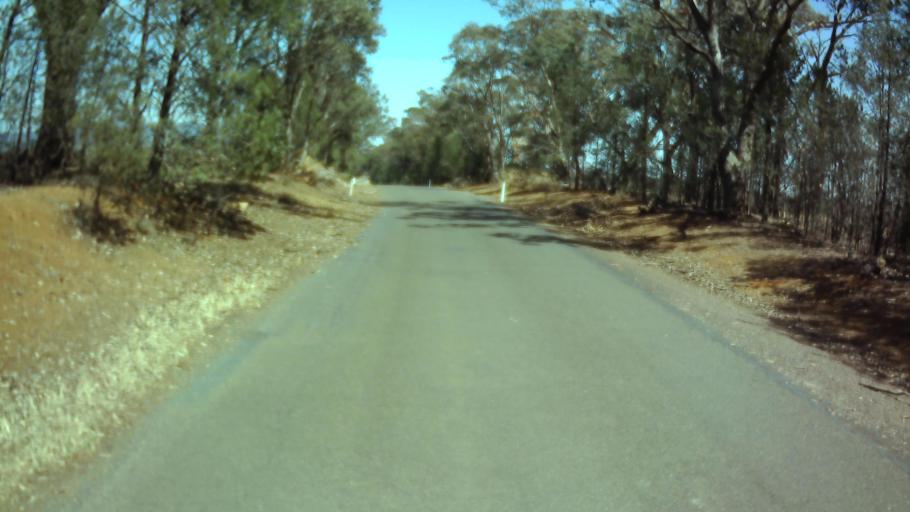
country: AU
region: New South Wales
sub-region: Weddin
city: Grenfell
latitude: -33.8706
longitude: 148.0970
